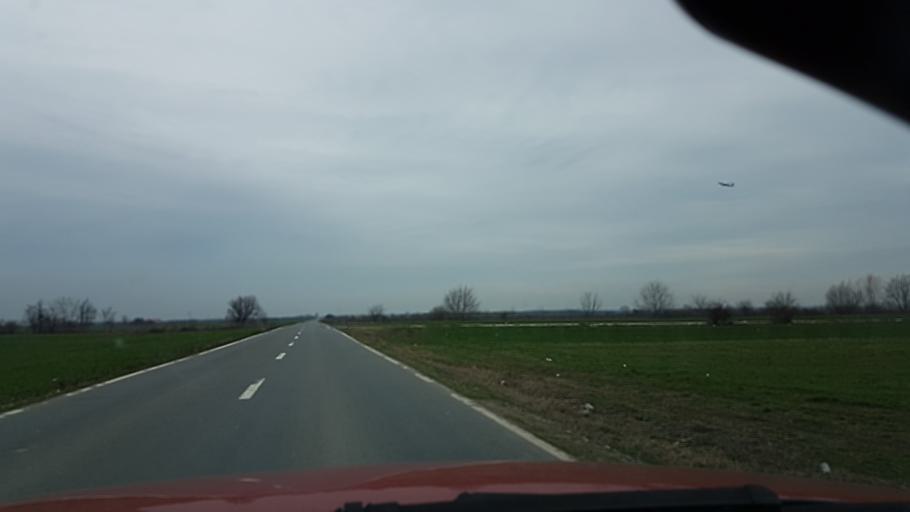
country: RO
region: Ilfov
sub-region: Comuna Tunari
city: Tunari
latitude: 44.5826
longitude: 26.1385
